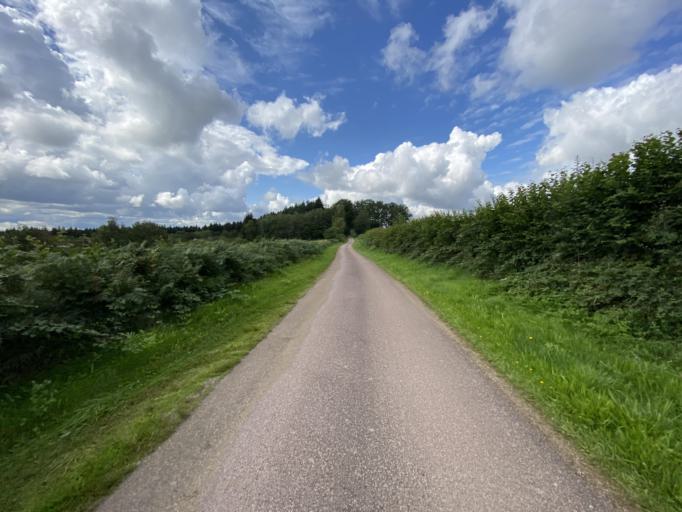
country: FR
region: Bourgogne
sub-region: Departement de la Cote-d'Or
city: Saulieu
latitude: 47.2742
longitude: 4.1916
